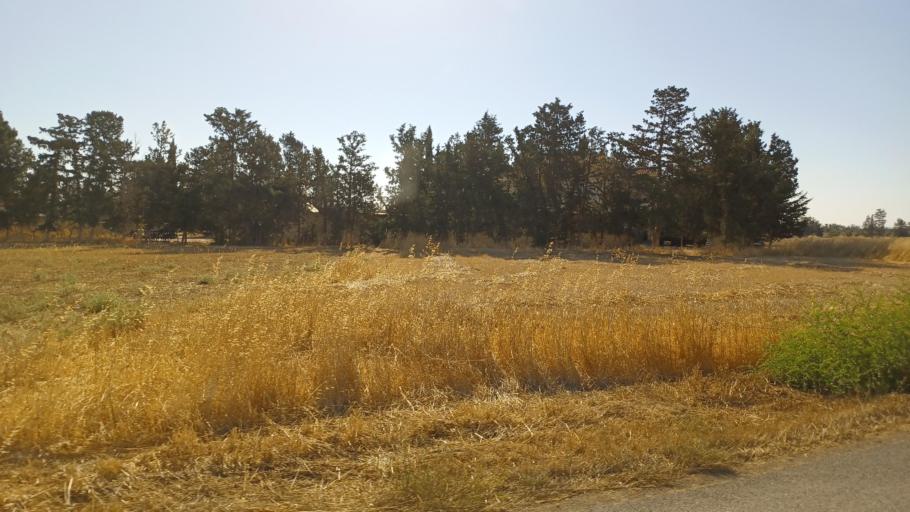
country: CY
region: Larnaka
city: Pergamos
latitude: 35.0358
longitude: 33.7017
